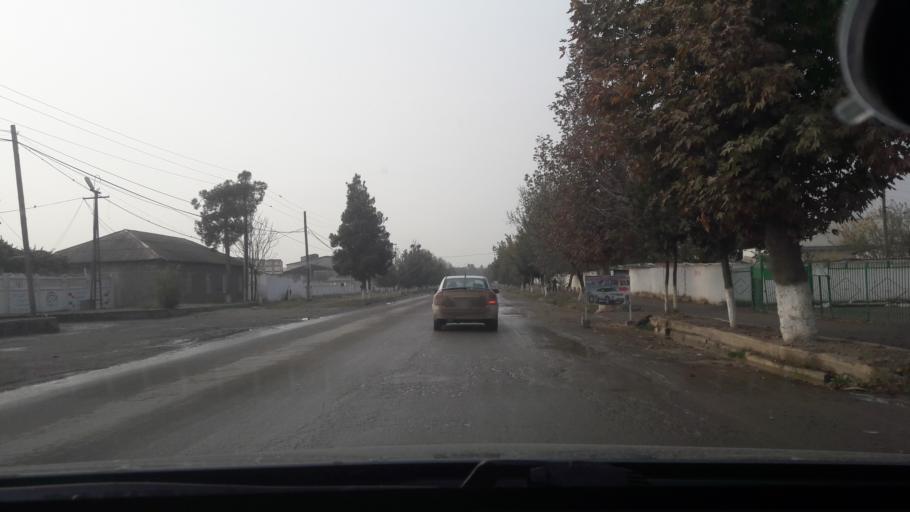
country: TJ
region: Khatlon
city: Abdurahmoni Jomi
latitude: 37.9841
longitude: 68.6996
